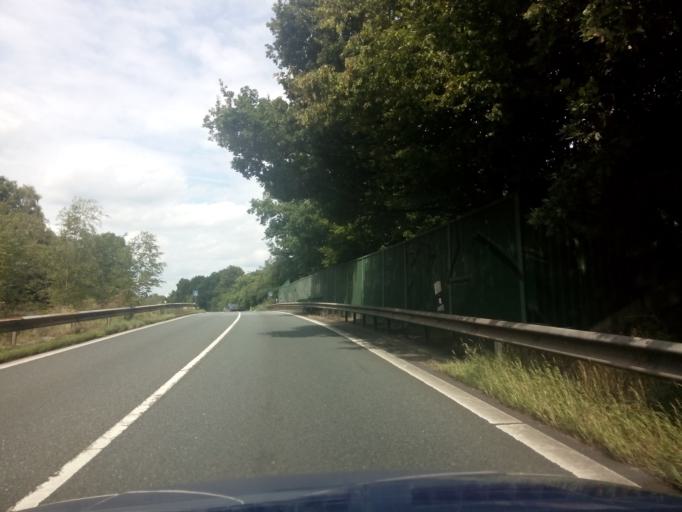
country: DE
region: Lower Saxony
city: Ritterhude
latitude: 53.1766
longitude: 8.7148
